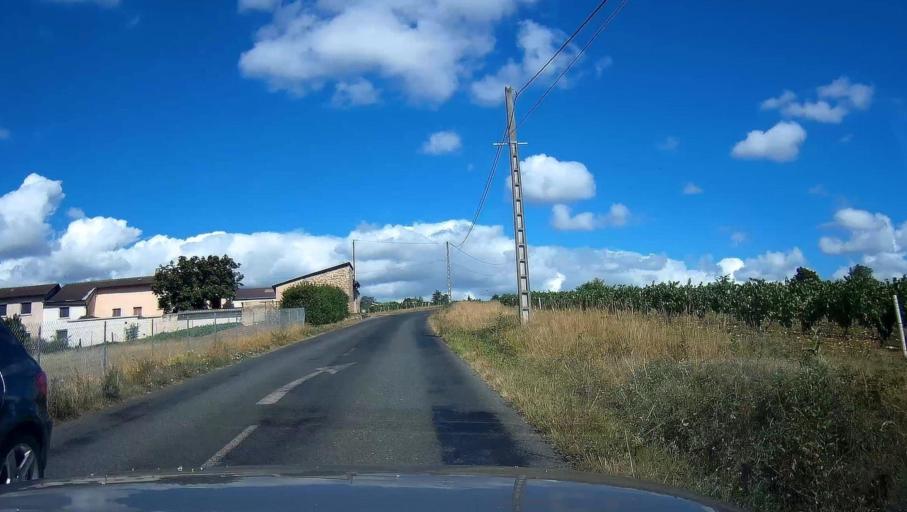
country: FR
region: Rhone-Alpes
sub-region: Departement du Rhone
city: Pommiers
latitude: 45.9499
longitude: 4.7006
